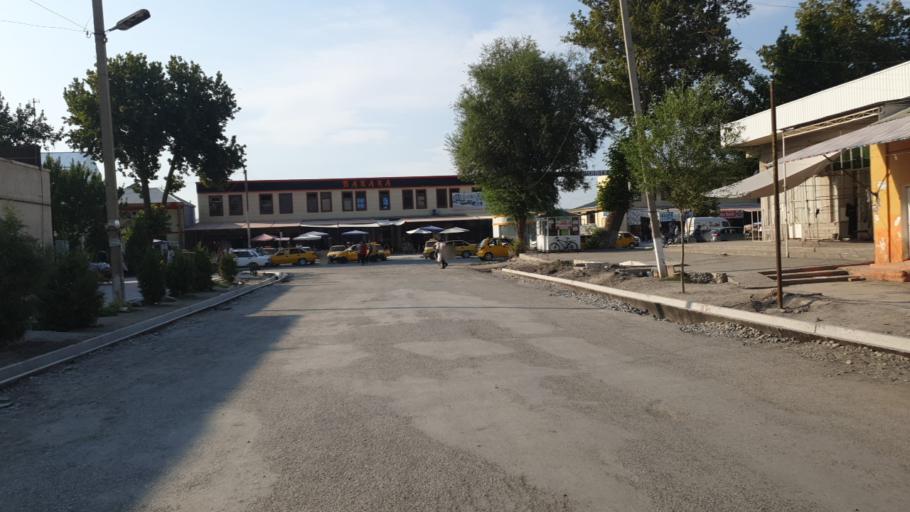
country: UZ
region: Fergana
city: Yaypan
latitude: 40.3804
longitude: 70.8103
